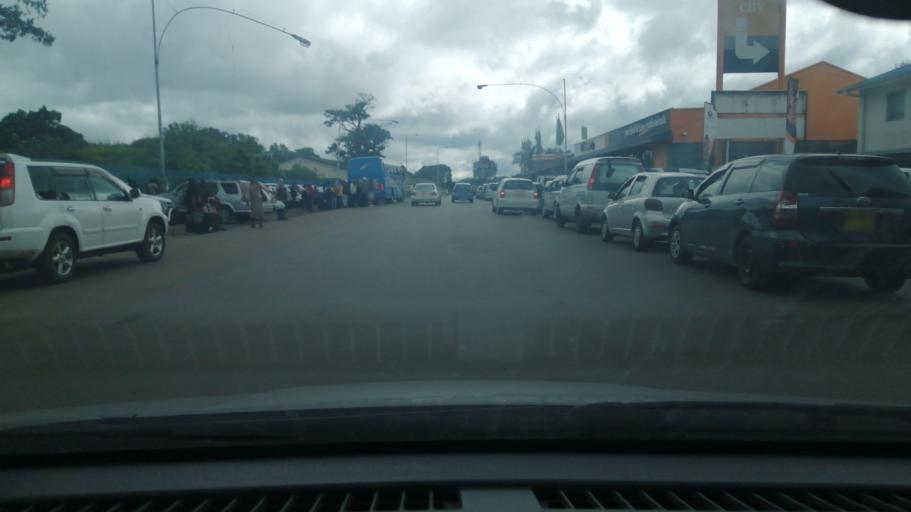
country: ZW
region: Harare
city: Harare
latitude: -17.8306
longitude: 31.0574
